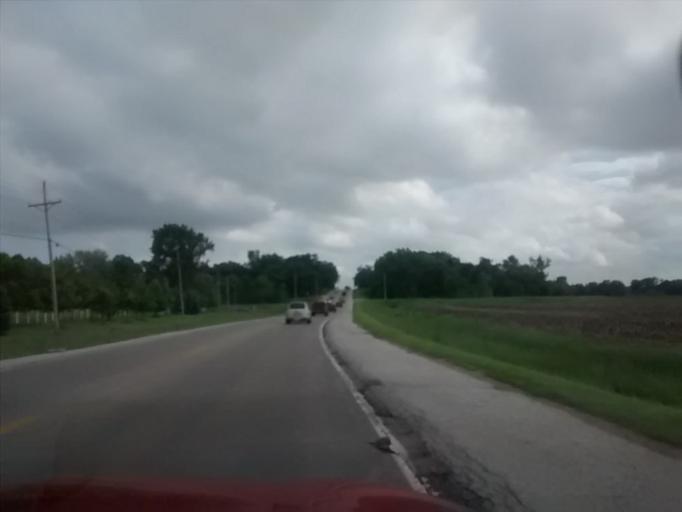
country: US
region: Nebraska
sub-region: Sarpy County
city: Offutt Air Force Base
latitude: 41.1570
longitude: -95.9666
